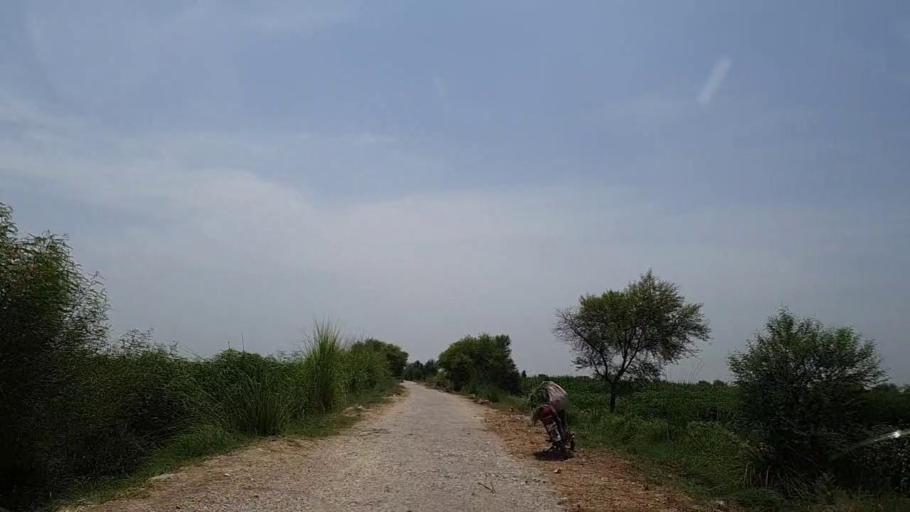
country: PK
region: Sindh
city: Khanpur
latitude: 27.8328
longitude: 69.4836
